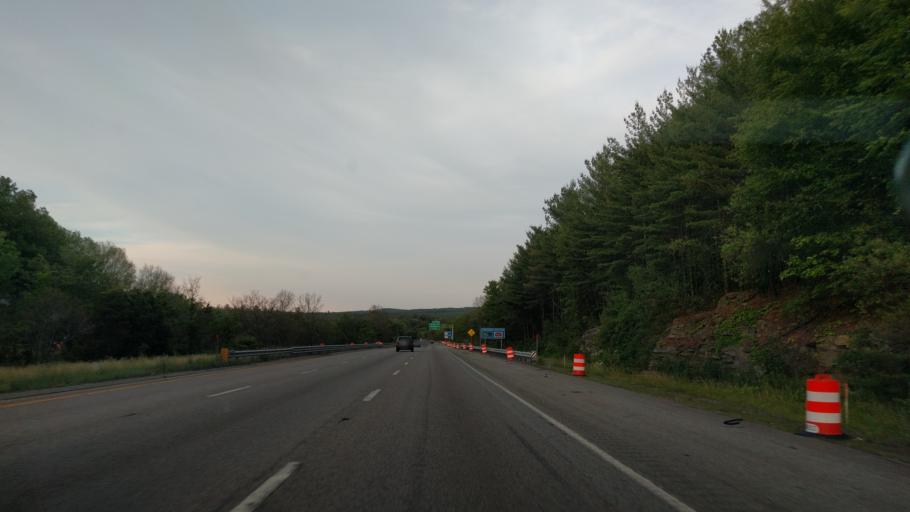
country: US
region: Massachusetts
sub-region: Worcester County
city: Northborough
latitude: 42.3424
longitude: -71.6395
